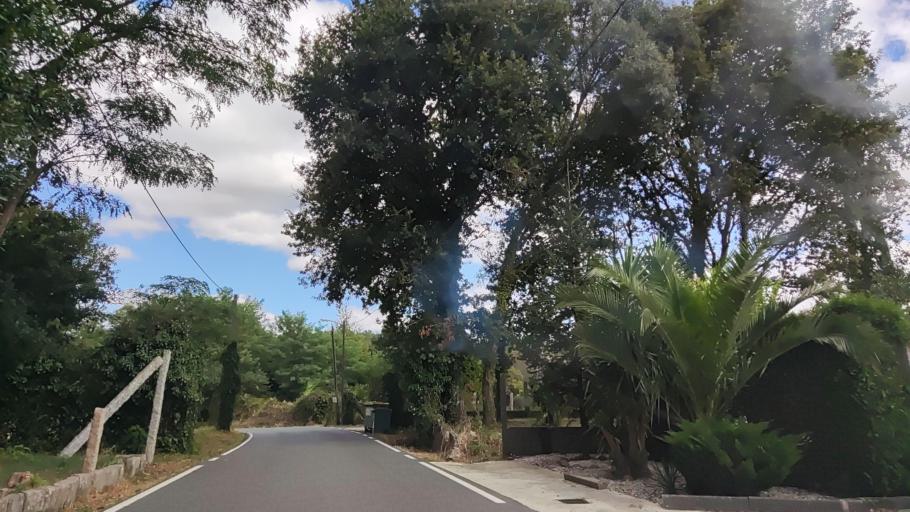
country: ES
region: Galicia
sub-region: Provincia da Coruna
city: Rois
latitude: 42.7812
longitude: -8.6683
